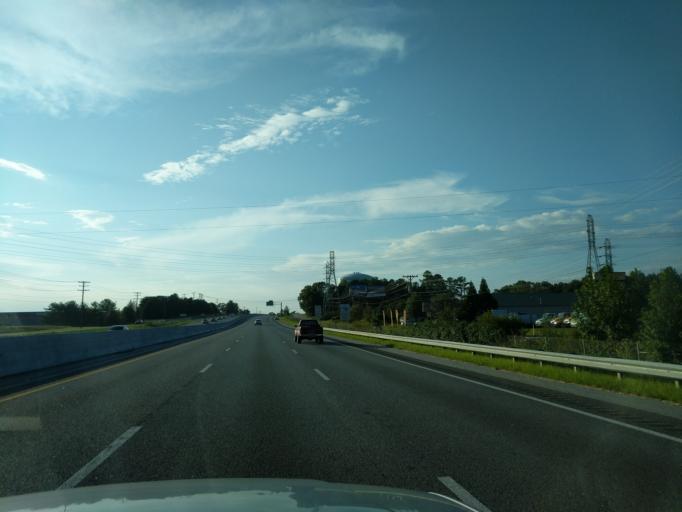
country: US
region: South Carolina
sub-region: Greenville County
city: Fountain Inn
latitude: 34.6921
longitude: -82.2244
